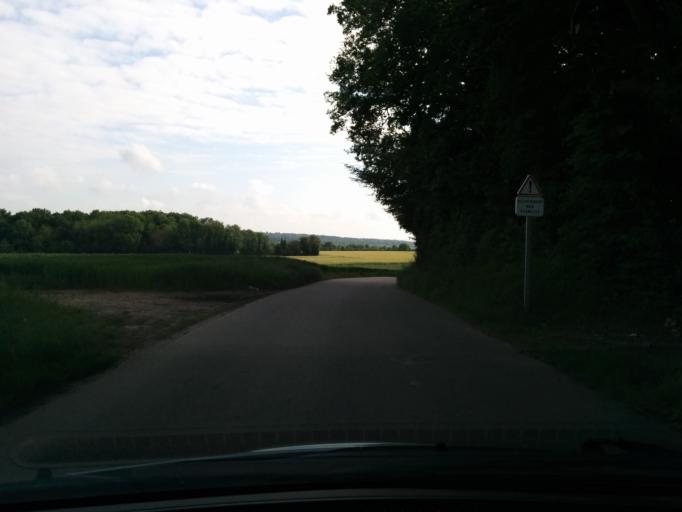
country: FR
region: Ile-de-France
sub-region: Departement des Yvelines
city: Oinville-sur-Montcient
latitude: 49.0202
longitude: 1.8314
